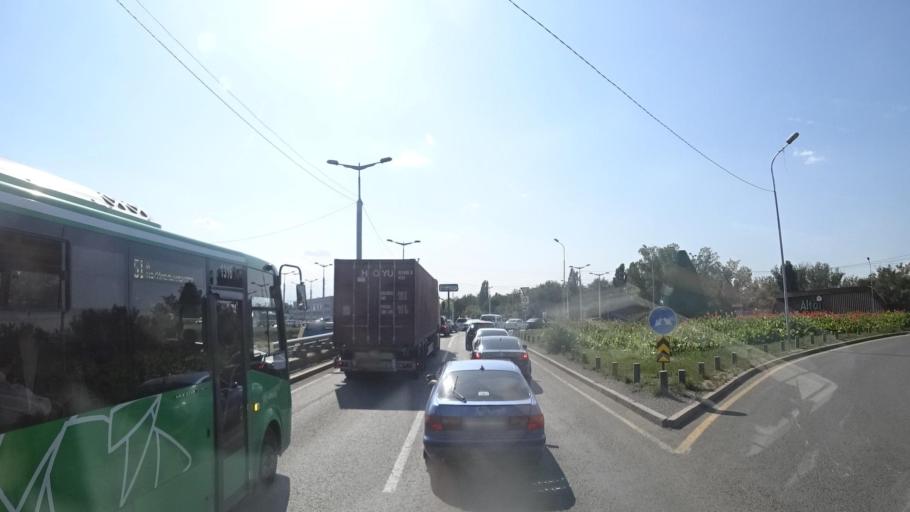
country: KZ
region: Almaty Oblysy
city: Pervomayskiy
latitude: 43.3413
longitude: 76.9849
